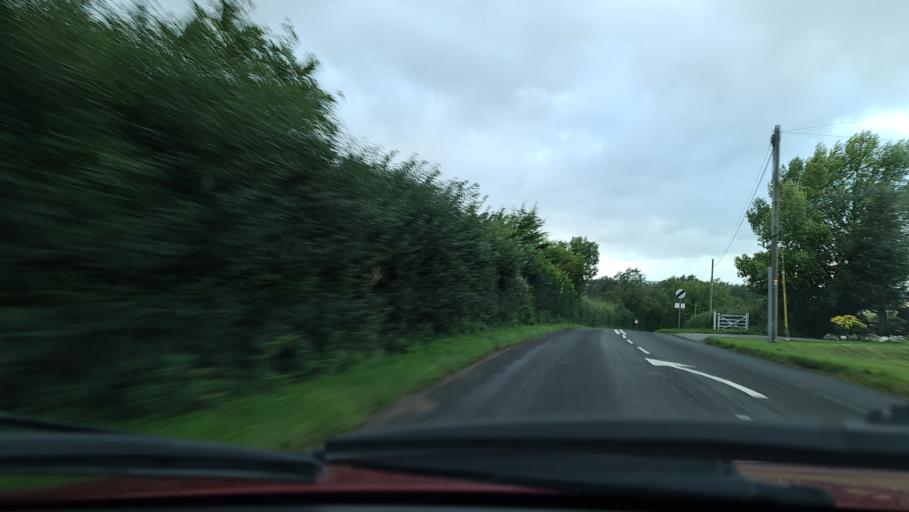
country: GB
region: England
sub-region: Buckinghamshire
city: Long Crendon
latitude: 51.7771
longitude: -1.0073
